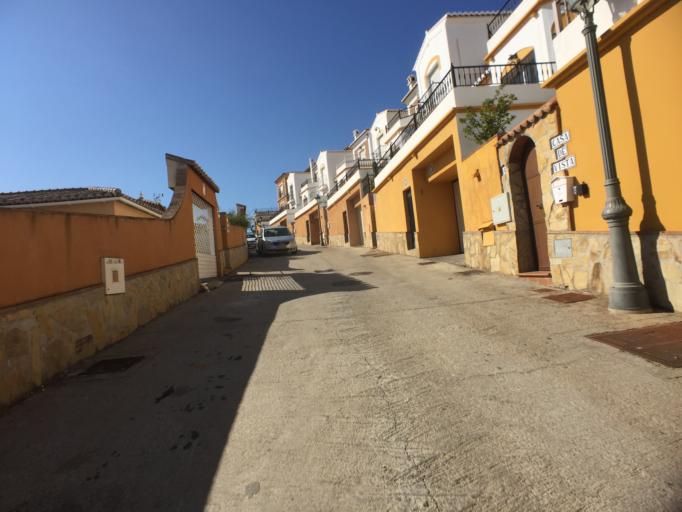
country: ES
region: Andalusia
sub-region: Provincia de Malaga
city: Nerja
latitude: 36.7455
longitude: -3.9065
